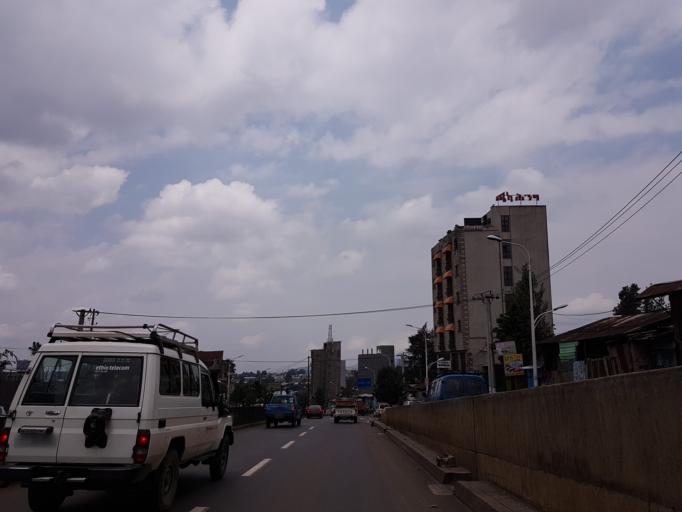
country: ET
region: Adis Abeba
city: Addis Ababa
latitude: 9.0099
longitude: 38.7340
